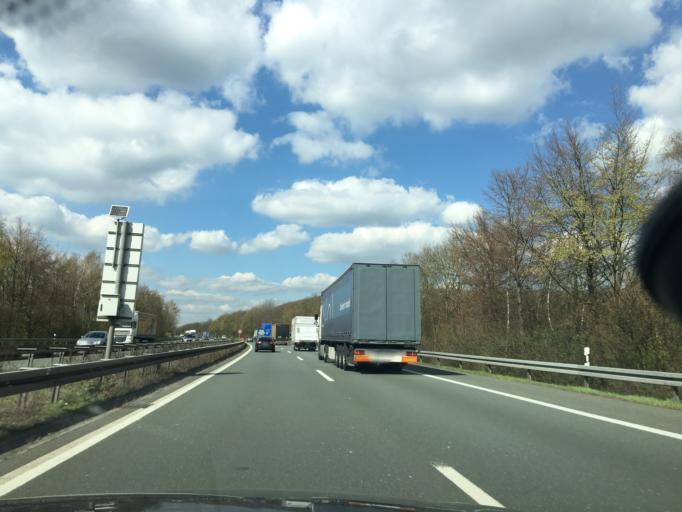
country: DE
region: North Rhine-Westphalia
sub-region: Regierungsbezirk Arnsberg
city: Wilnsdorf
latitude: 50.8069
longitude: 8.0993
